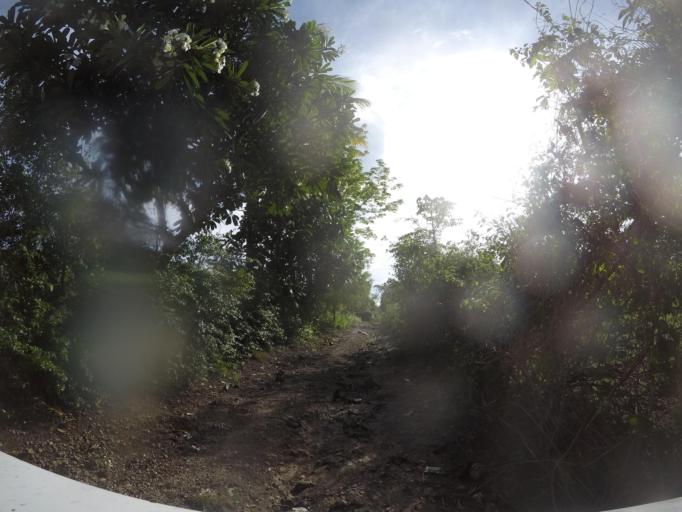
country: TL
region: Baucau
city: Baucau
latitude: -8.5057
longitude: 126.4480
